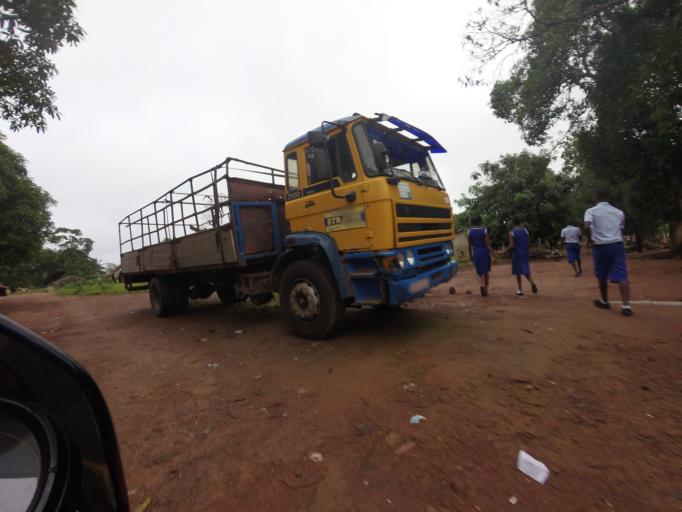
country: SL
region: Northern Province
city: Kambia
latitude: 9.0131
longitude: -12.9479
